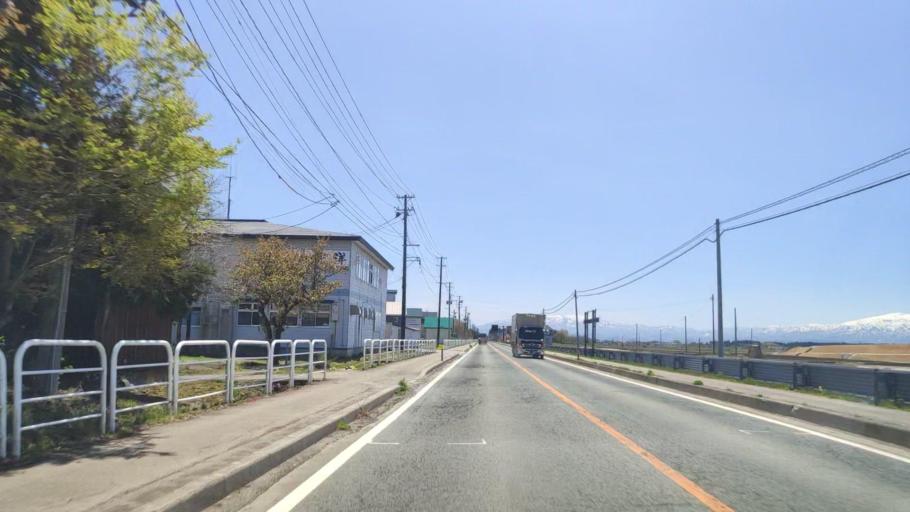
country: JP
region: Yamagata
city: Shinjo
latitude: 38.8350
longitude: 140.3292
